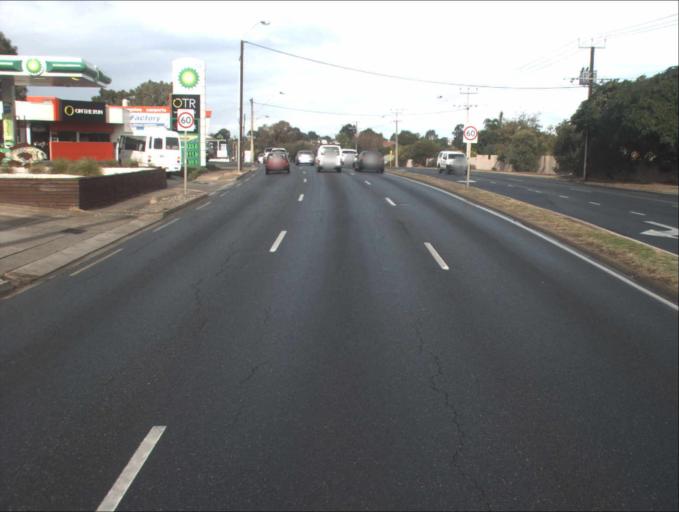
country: AU
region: South Australia
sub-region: Tea Tree Gully
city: Modbury
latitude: -34.8457
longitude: 138.6707
